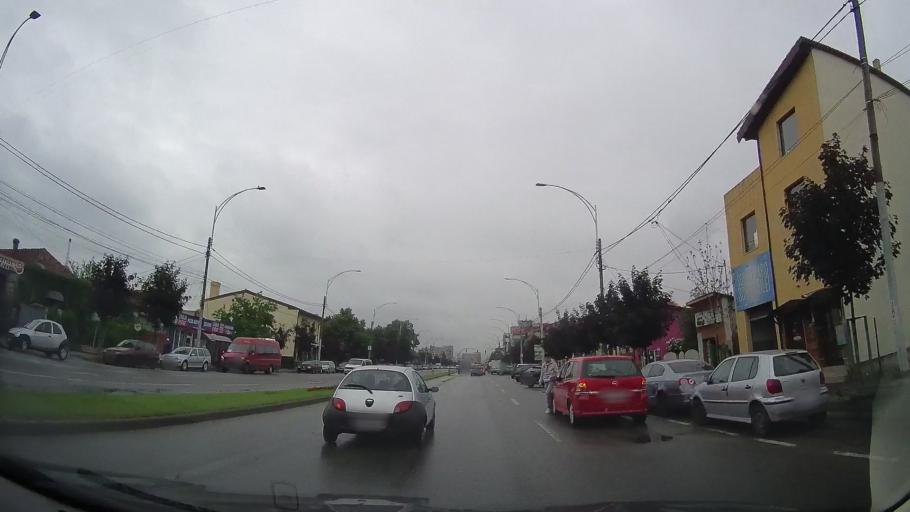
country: RO
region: Mehedinti
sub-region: Municipiul Drobeta-Turnu Severin
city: Drobeta-Turnu Severin
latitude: 44.6316
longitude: 22.6496
